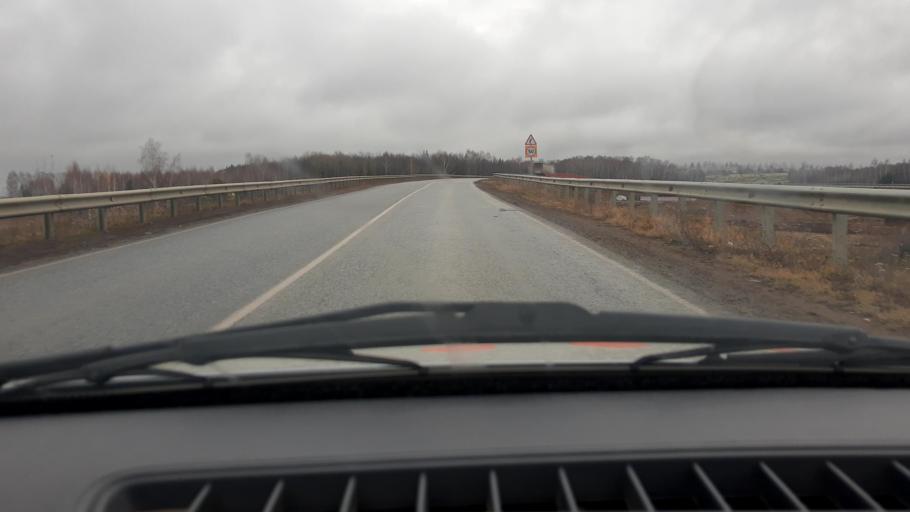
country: RU
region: Bashkortostan
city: Iglino
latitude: 54.7443
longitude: 56.3020
